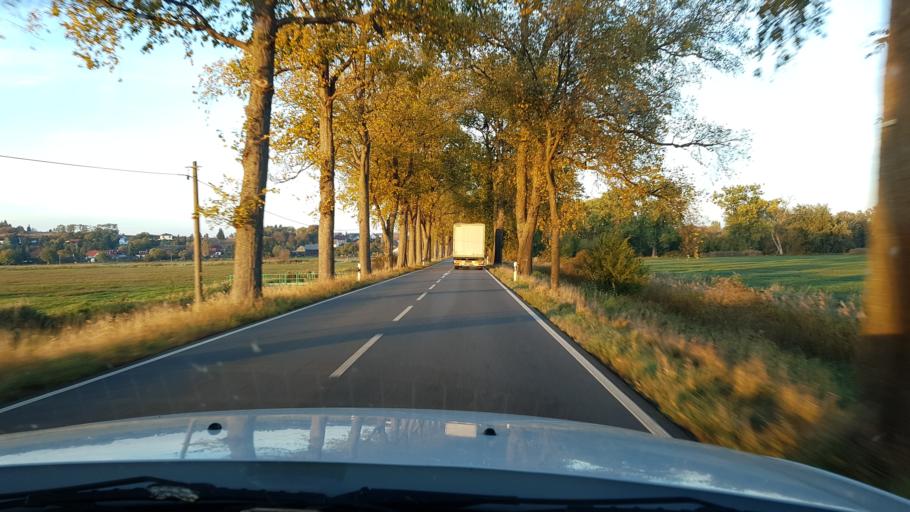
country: DE
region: Brandenburg
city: Gartz
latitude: 53.2068
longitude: 14.3650
